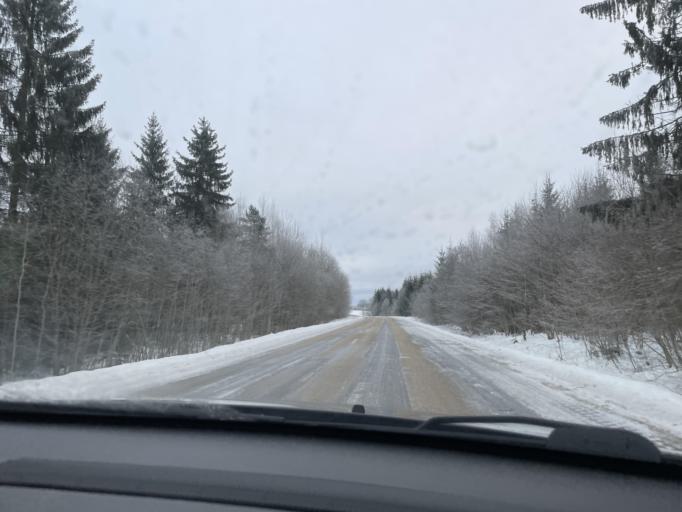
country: LV
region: Rezekne
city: Rezekne
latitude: 56.4990
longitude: 27.3887
